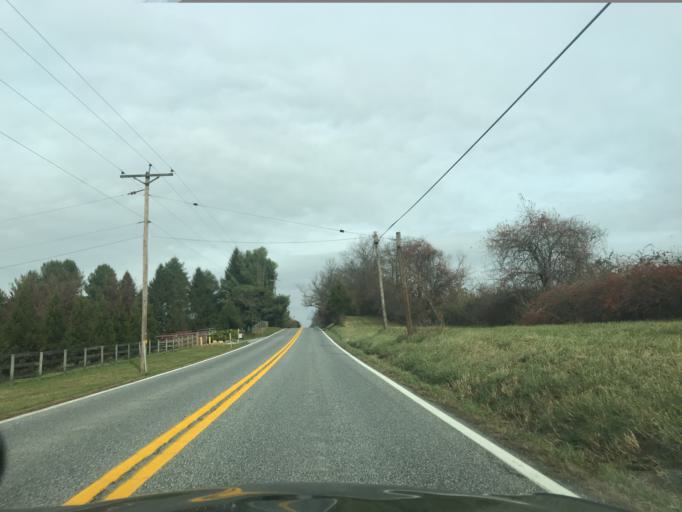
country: US
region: Maryland
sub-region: Harford County
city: Jarrettsville
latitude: 39.5704
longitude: -76.5209
